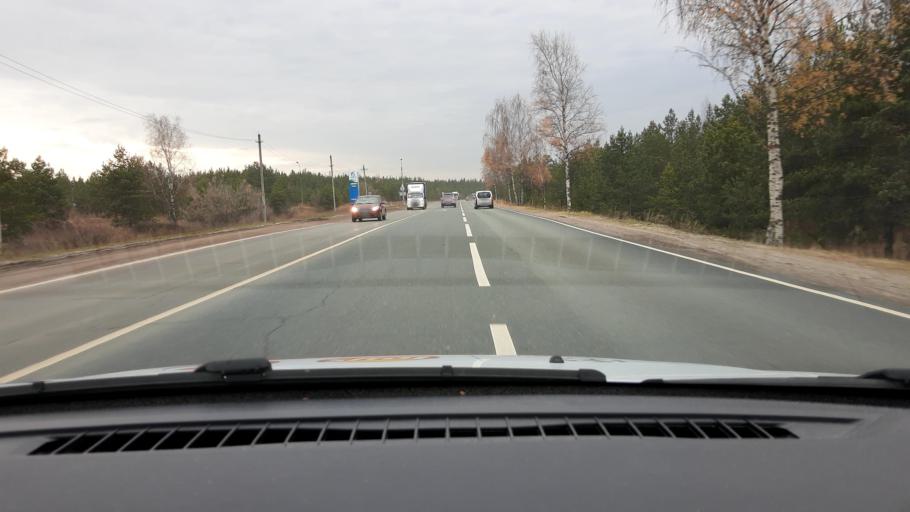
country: RU
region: Nizjnij Novgorod
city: Dzerzhinsk
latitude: 56.2786
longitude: 43.4752
